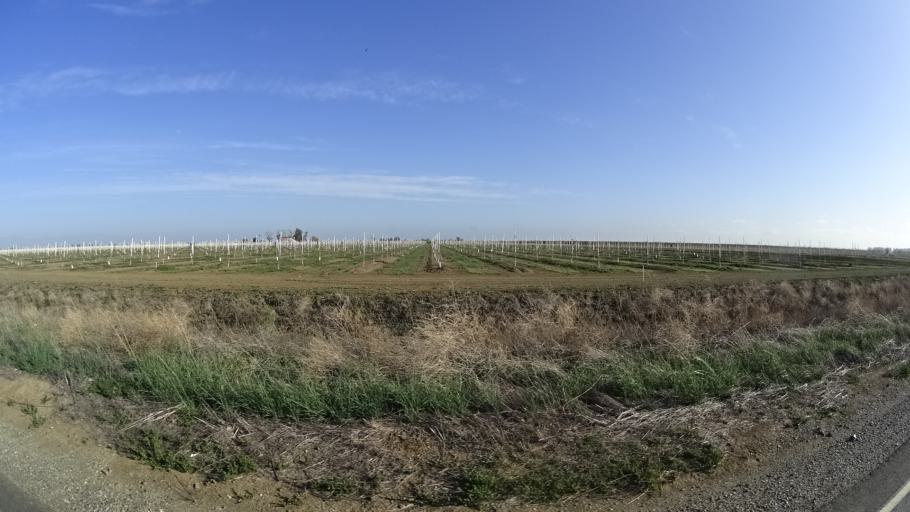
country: US
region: California
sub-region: Glenn County
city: Willows
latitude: 39.5824
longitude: -122.2366
